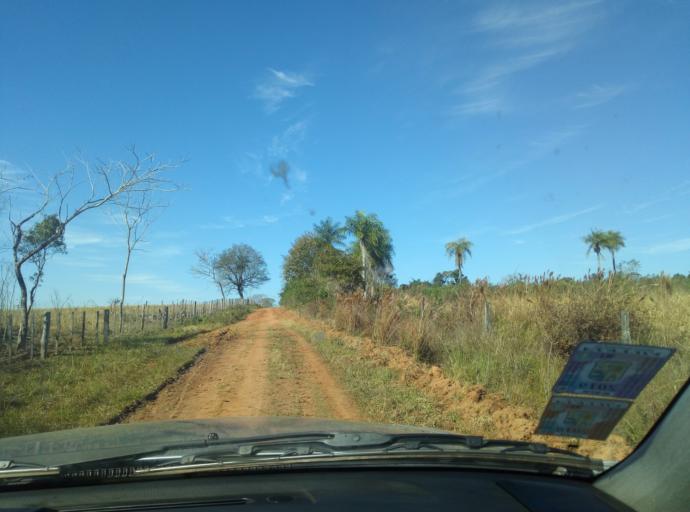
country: PY
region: Caaguazu
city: Carayao
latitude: -25.1690
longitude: -56.3068
